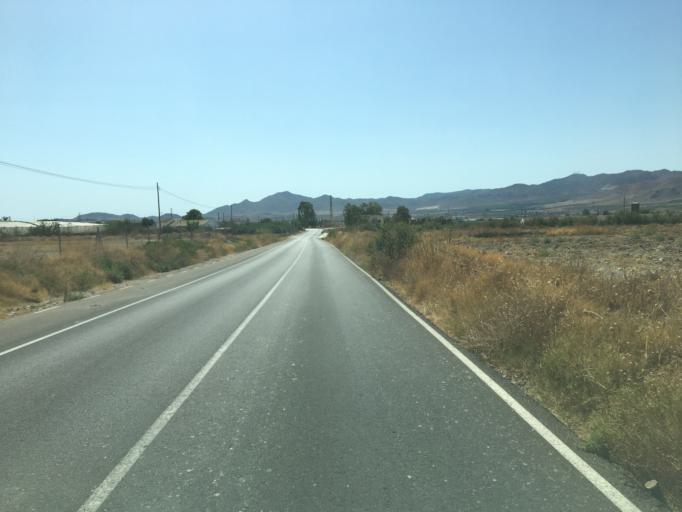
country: ES
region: Andalusia
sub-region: Provincia de Almeria
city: Huercal-Overa
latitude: 37.4205
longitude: -1.9171
